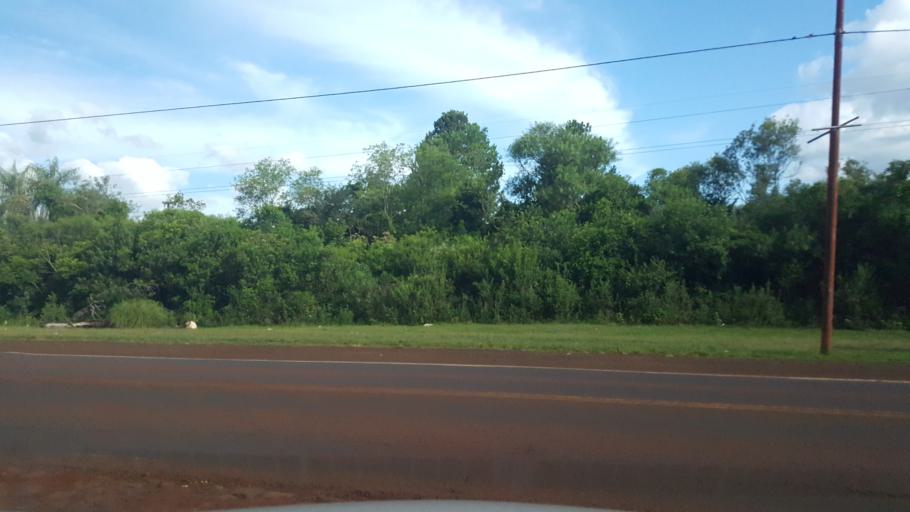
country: AR
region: Misiones
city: Santa Ana
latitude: -27.3788
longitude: -55.5792
